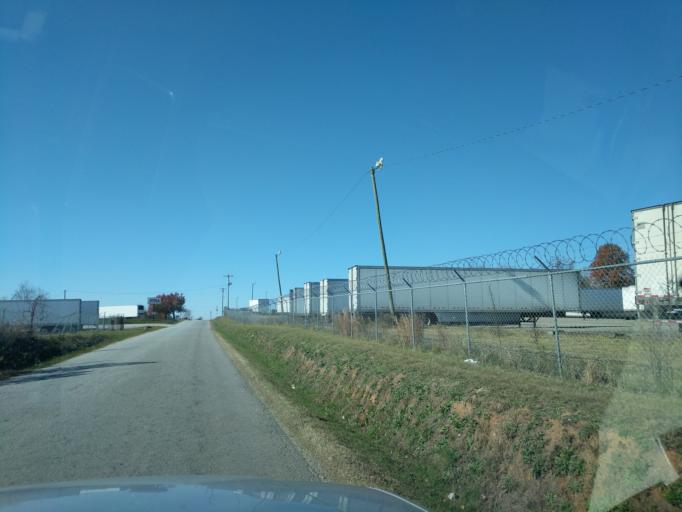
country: US
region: South Carolina
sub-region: Spartanburg County
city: Duncan
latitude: 34.8881
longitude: -82.1506
